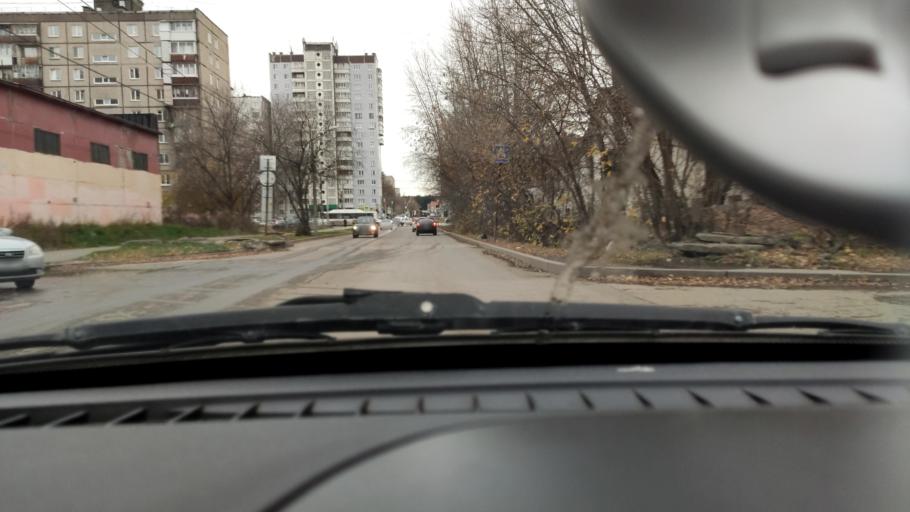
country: RU
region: Perm
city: Kondratovo
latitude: 57.9992
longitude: 56.1468
